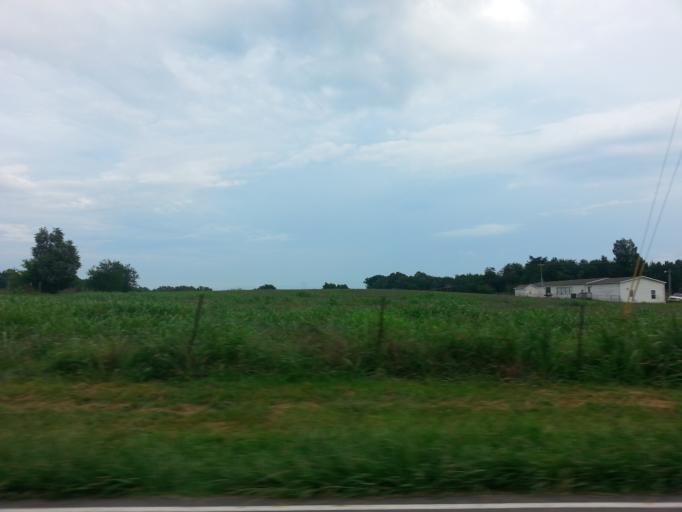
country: US
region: Tennessee
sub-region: Loudon County
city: Greenback
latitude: 35.6534
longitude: -84.1869
